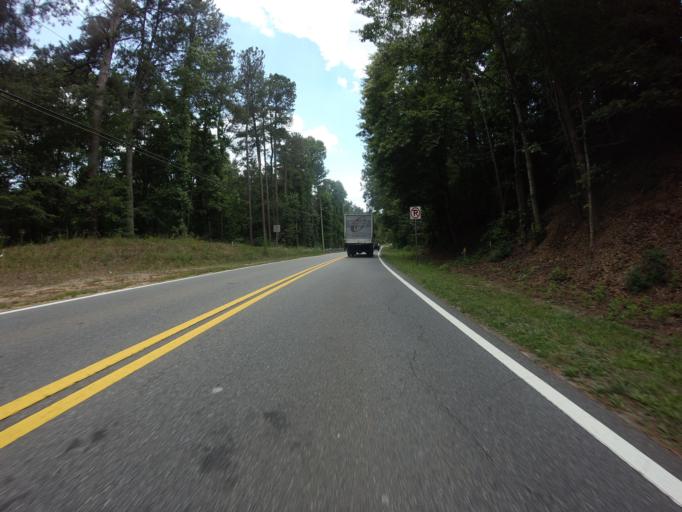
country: US
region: Georgia
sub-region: Gwinnett County
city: Norcross
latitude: 33.9896
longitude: -84.2603
